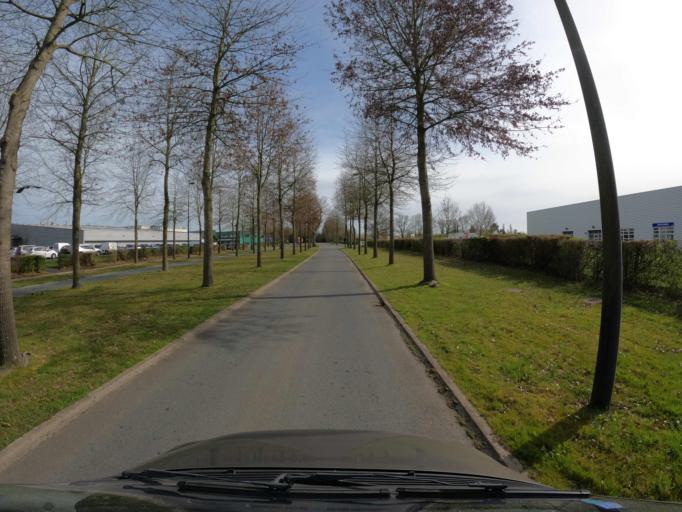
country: FR
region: Pays de la Loire
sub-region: Departement de la Vendee
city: Bouffere
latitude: 46.9537
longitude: -1.3512
